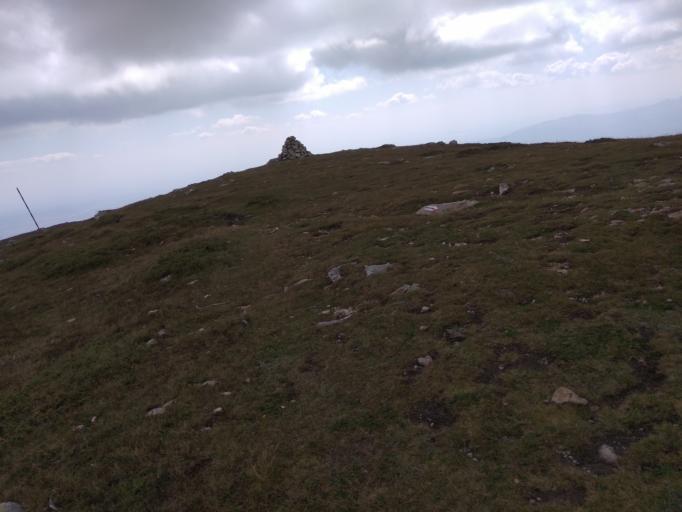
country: BG
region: Plovdiv
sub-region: Obshtina Karlovo
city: Karlovo
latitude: 42.7203
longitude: 24.7810
